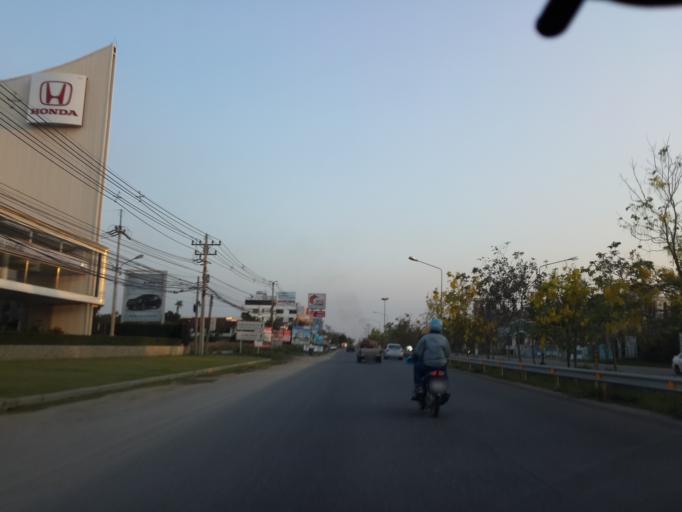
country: TH
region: Chon Buri
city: Phatthaya
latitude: 12.8383
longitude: 100.9121
